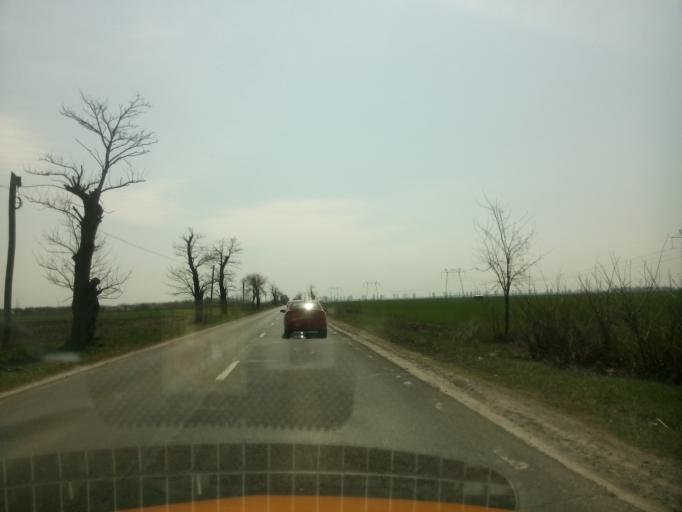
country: RO
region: Calarasi
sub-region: Comuna Frumusani
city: Frumusani
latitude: 44.2621
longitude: 26.3552
